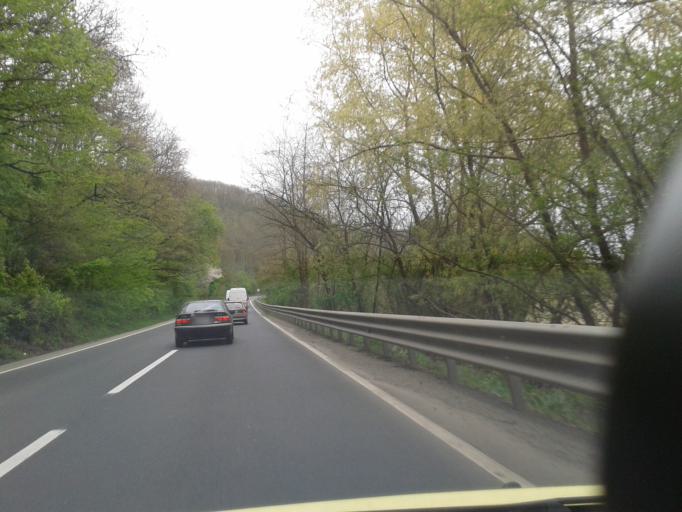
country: RO
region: Arad
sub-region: Comuna Bata
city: Bata
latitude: 46.0740
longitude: 22.0344
